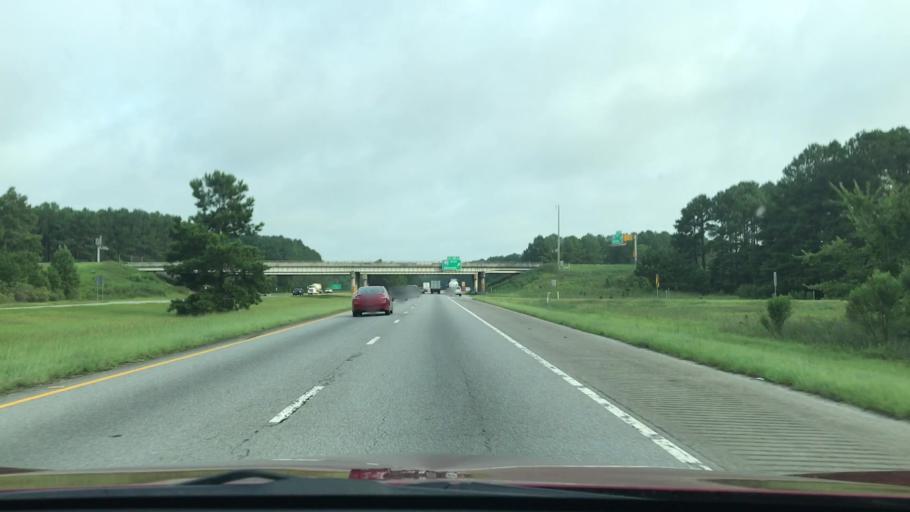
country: US
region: South Carolina
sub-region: Orangeburg County
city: Holly Hill
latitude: 33.3171
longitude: -80.5463
